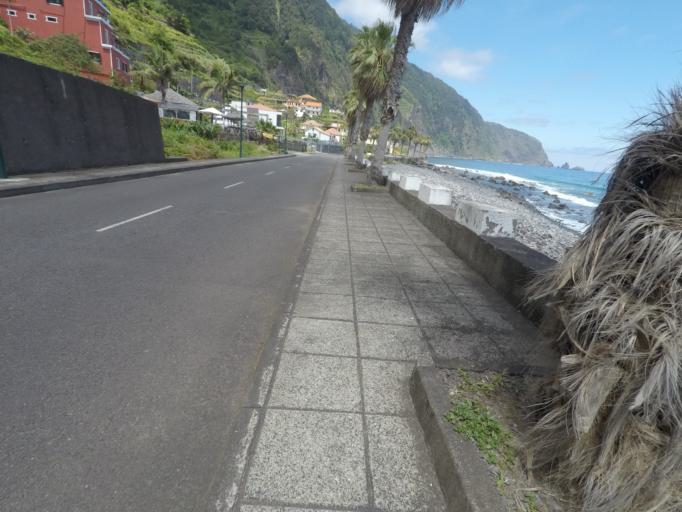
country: PT
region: Madeira
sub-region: Porto Moniz
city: Porto Moniz
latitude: 32.8257
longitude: -17.1174
